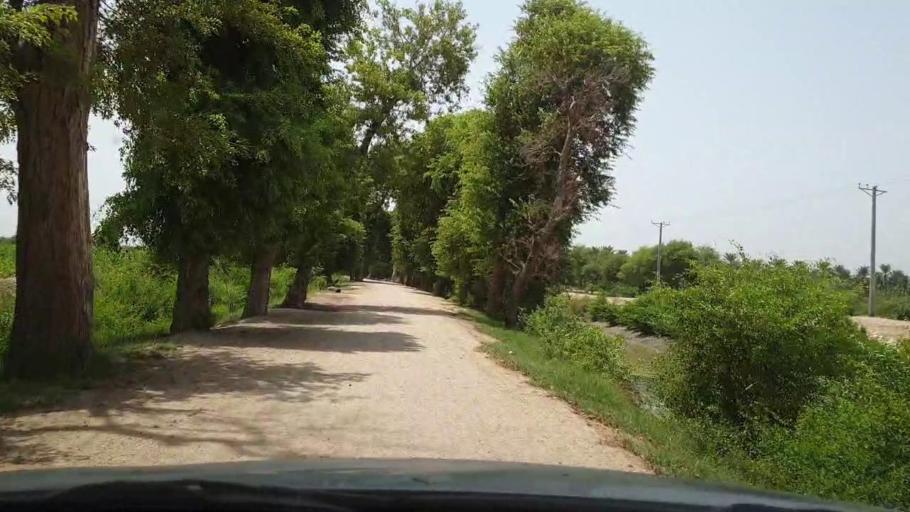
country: PK
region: Sindh
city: Pano Aqil
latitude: 27.8599
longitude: 69.0881
